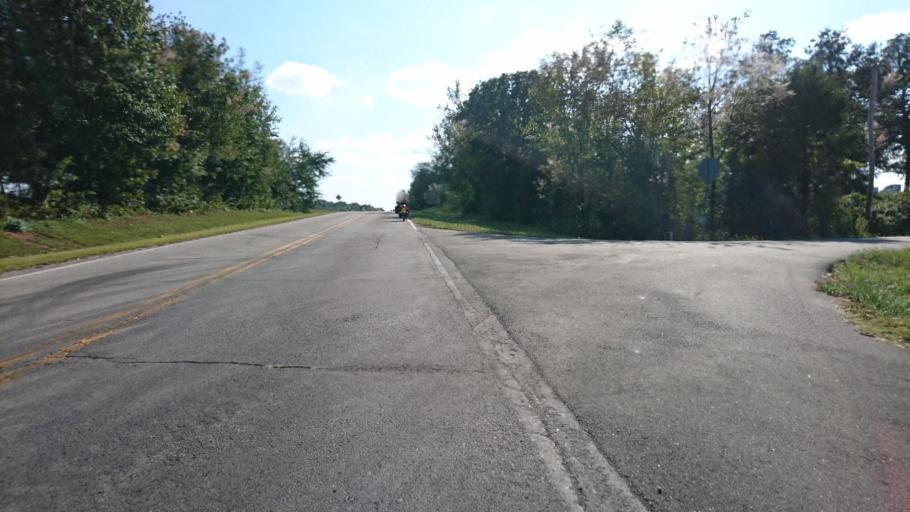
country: US
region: Missouri
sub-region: Laclede County
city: Lebanon
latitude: 37.6266
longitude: -92.6901
